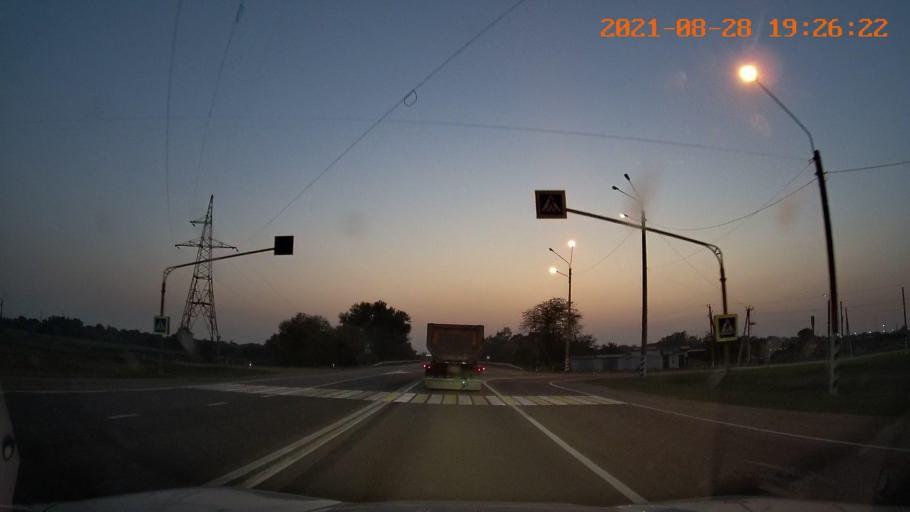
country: RU
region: Adygeya
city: Ponezhukay
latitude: 44.8781
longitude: 39.3951
